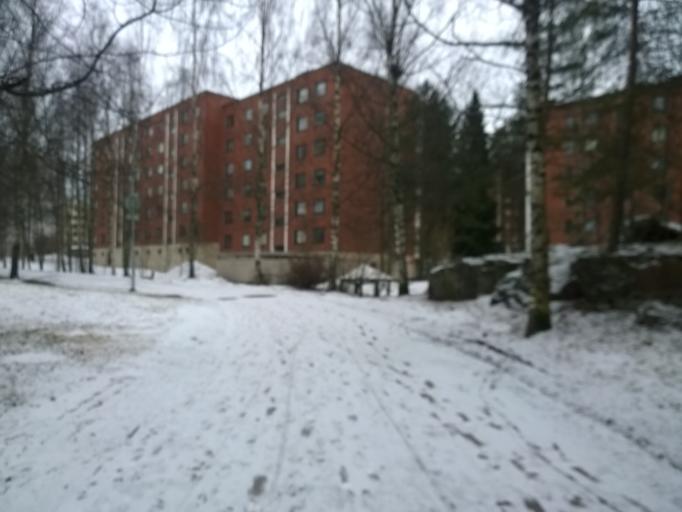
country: FI
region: Pirkanmaa
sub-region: Tampere
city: Tampere
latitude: 61.4474
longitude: 23.8391
